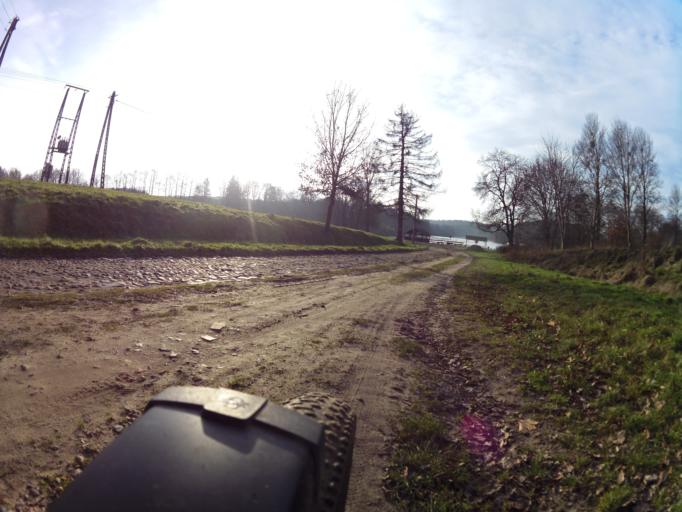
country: PL
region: West Pomeranian Voivodeship
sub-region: Powiat koszalinski
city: Polanow
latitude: 54.1570
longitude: 16.7323
